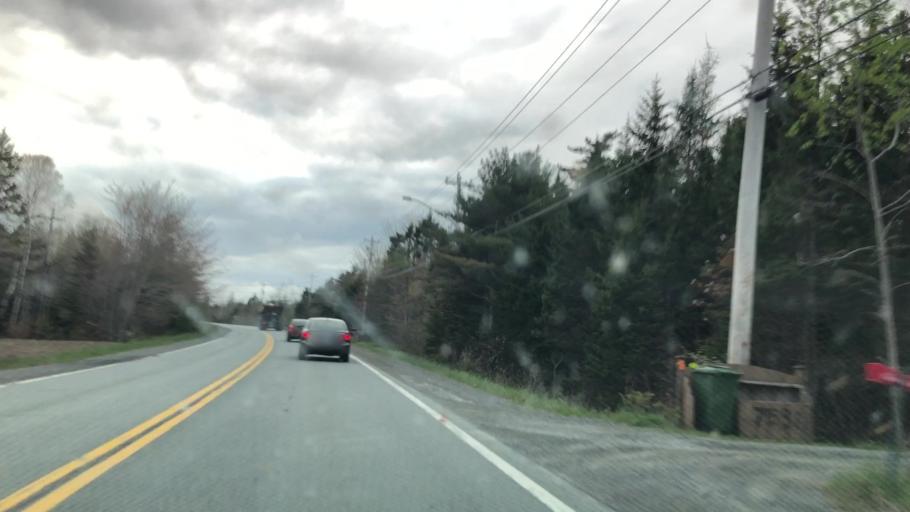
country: CA
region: Nova Scotia
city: Cole Harbour
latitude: 44.7833
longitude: -63.1693
